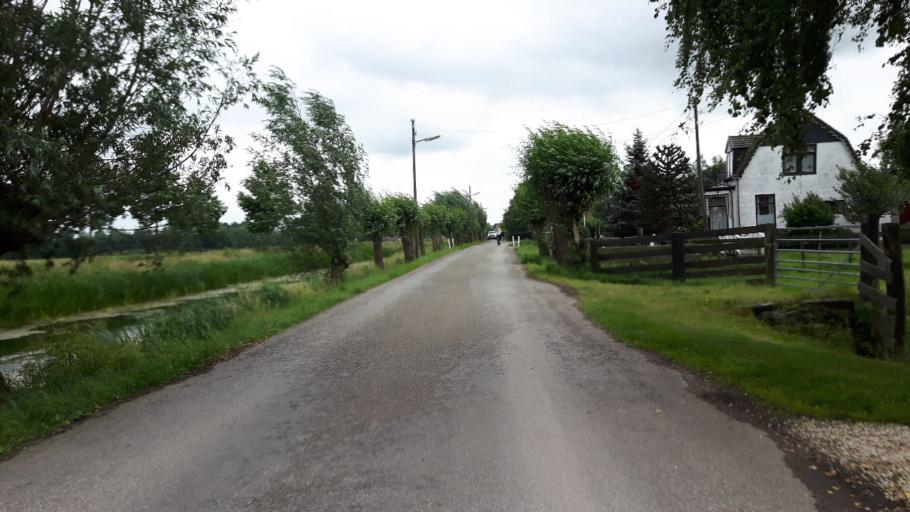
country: NL
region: Utrecht
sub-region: Gemeente Oudewater
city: Oudewater
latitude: 52.0388
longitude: 4.8577
